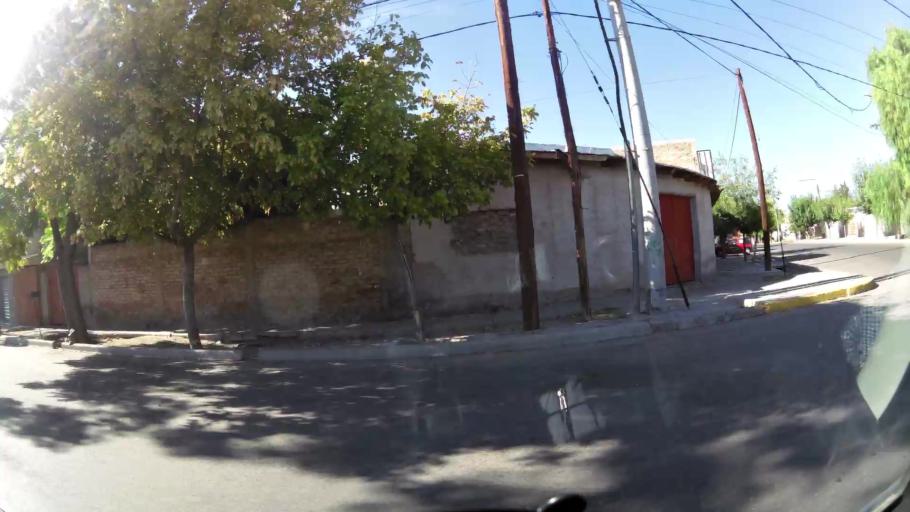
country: AR
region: Mendoza
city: Las Heras
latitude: -32.8727
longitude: -68.8690
